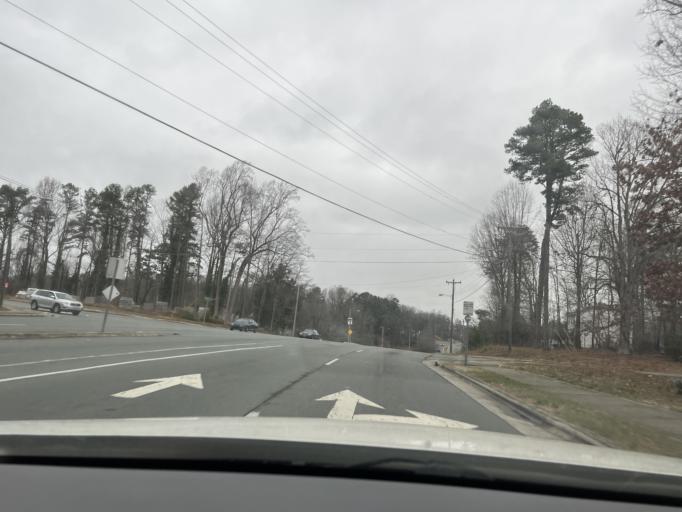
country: US
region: North Carolina
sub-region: Guilford County
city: Pleasant Garden
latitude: 36.0088
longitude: -79.7938
